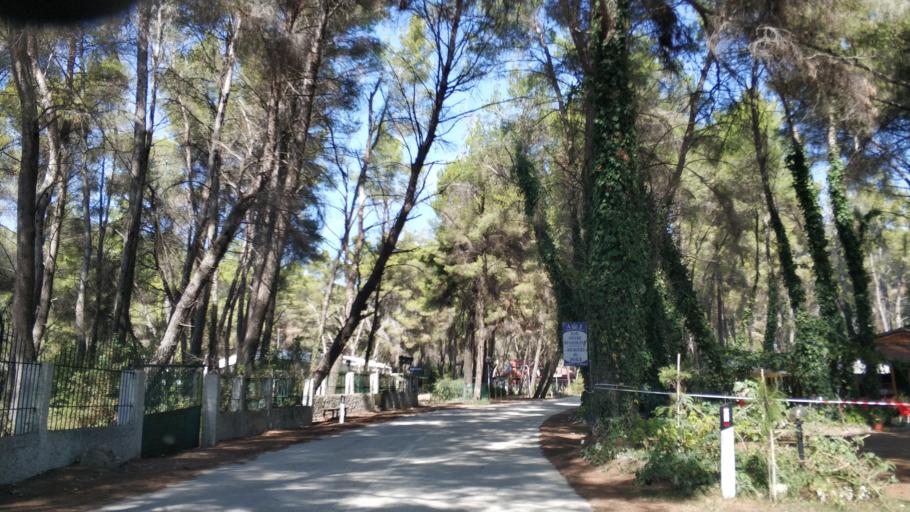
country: AL
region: Fier
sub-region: Rrethi i Lushnjes
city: Divjake
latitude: 40.9737
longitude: 19.4805
